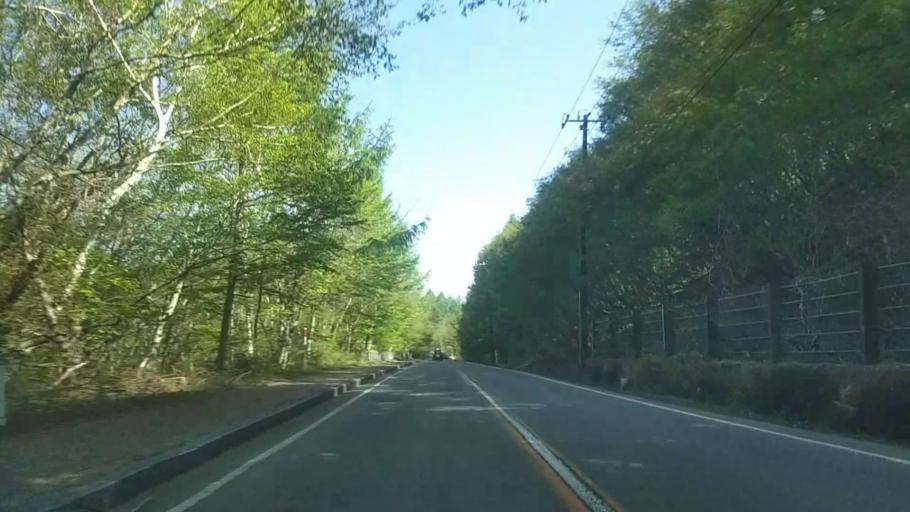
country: JP
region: Yamanashi
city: Nirasaki
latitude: 35.9218
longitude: 138.4051
